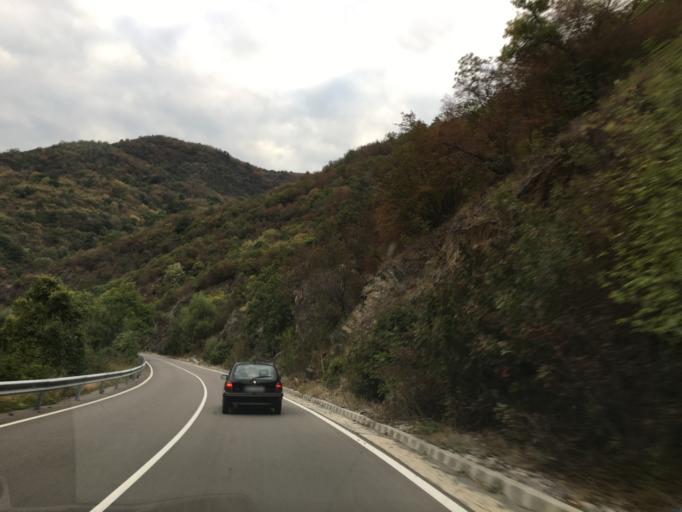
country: BG
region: Sofiya
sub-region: Obshtina Svoge
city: Bov
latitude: 43.0448
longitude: 23.3544
